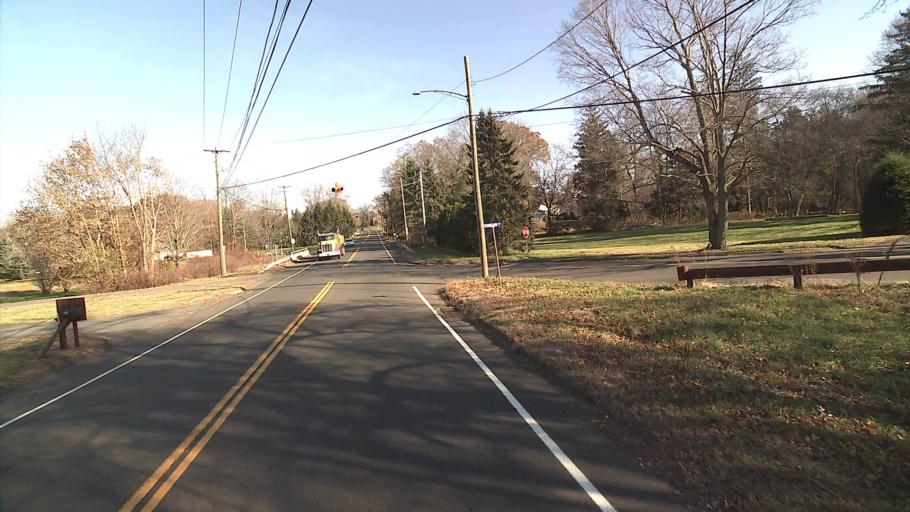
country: US
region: Connecticut
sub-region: New Haven County
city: North Haven
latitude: 41.3531
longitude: -72.8465
